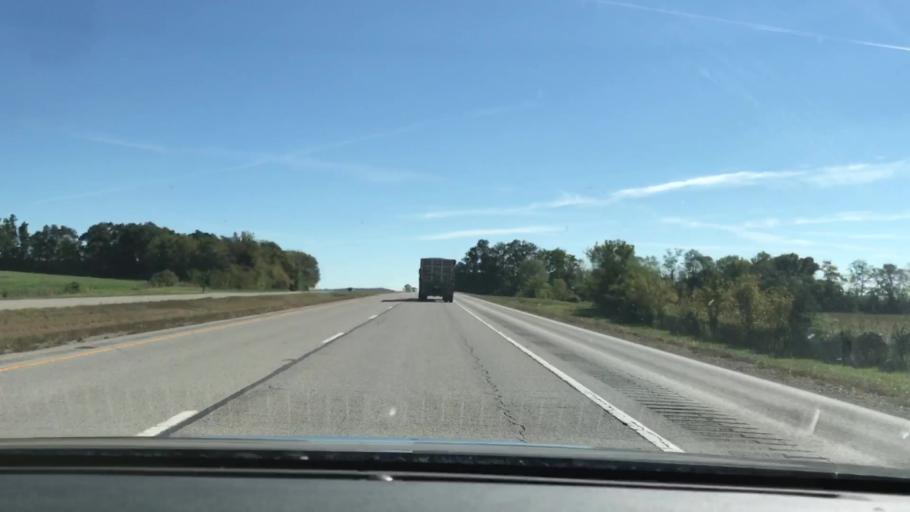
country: US
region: Kentucky
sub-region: Todd County
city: Elkton
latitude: 36.8462
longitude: -87.2944
